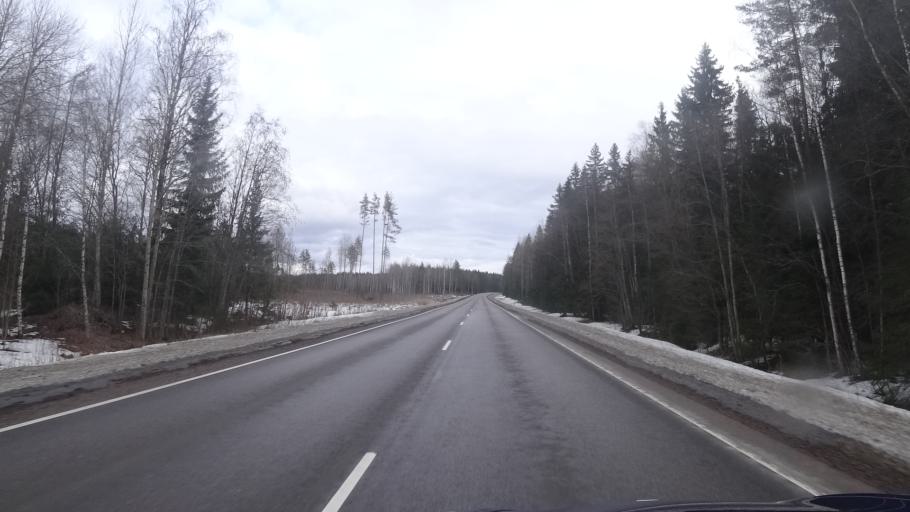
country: FI
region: Kymenlaakso
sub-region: Kouvola
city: Elimaeki
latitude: 60.6915
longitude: 26.6319
